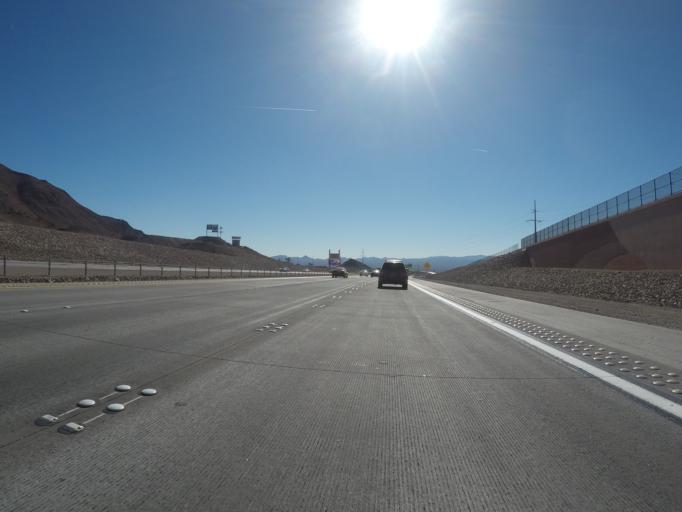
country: US
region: Nevada
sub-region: Clark County
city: Boulder City
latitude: 35.9771
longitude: -114.9157
